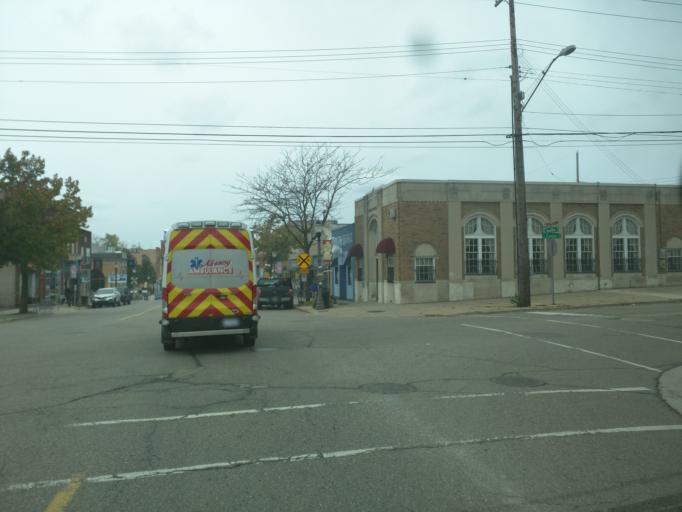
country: US
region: Michigan
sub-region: Ingham County
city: Lansing
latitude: 42.7474
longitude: -84.5478
